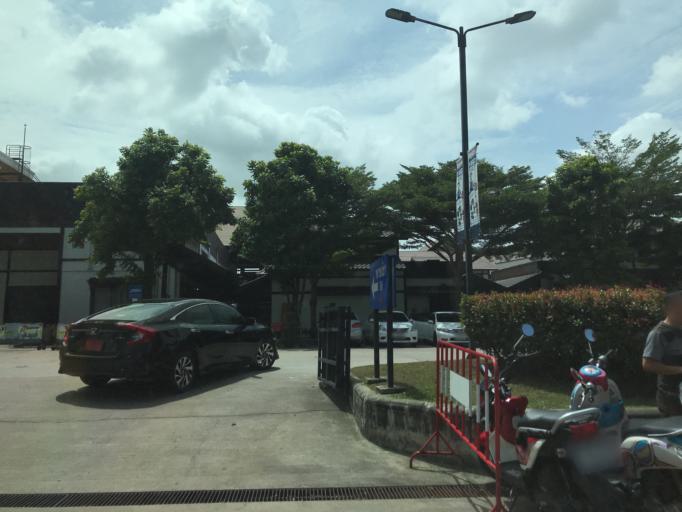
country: TH
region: Chon Buri
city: Si Racha
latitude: 13.1538
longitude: 100.9828
